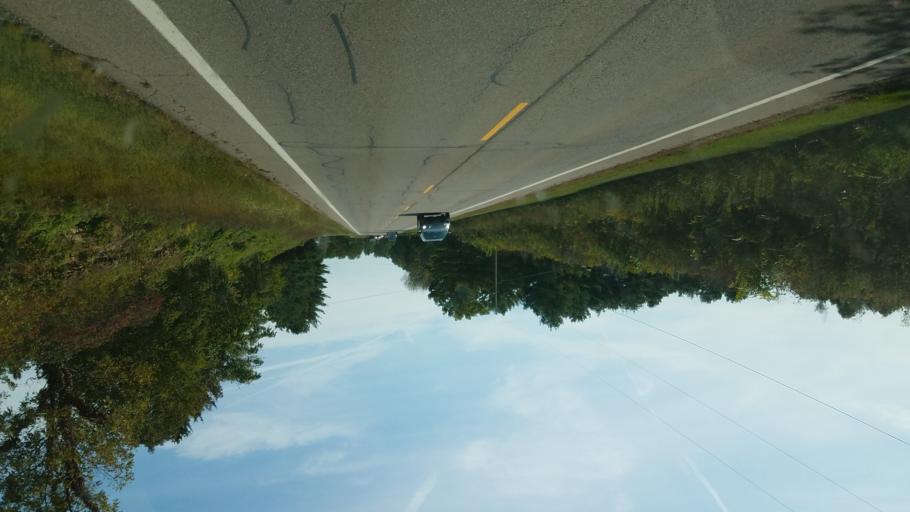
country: US
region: Ohio
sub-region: Knox County
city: Gambier
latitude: 40.3824
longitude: -82.4218
